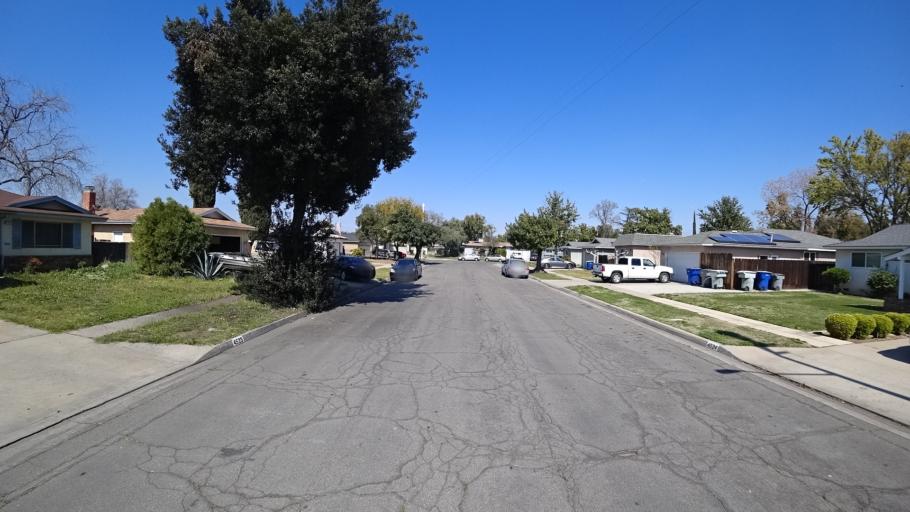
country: US
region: California
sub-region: Fresno County
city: Tarpey Village
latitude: 36.8000
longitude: -119.7336
